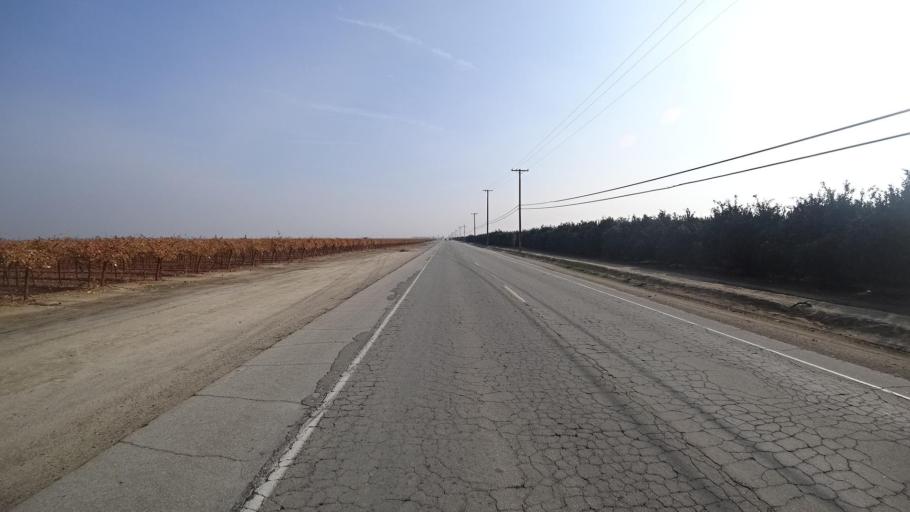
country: US
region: California
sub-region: Kern County
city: Weedpatch
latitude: 35.0933
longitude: -118.9572
